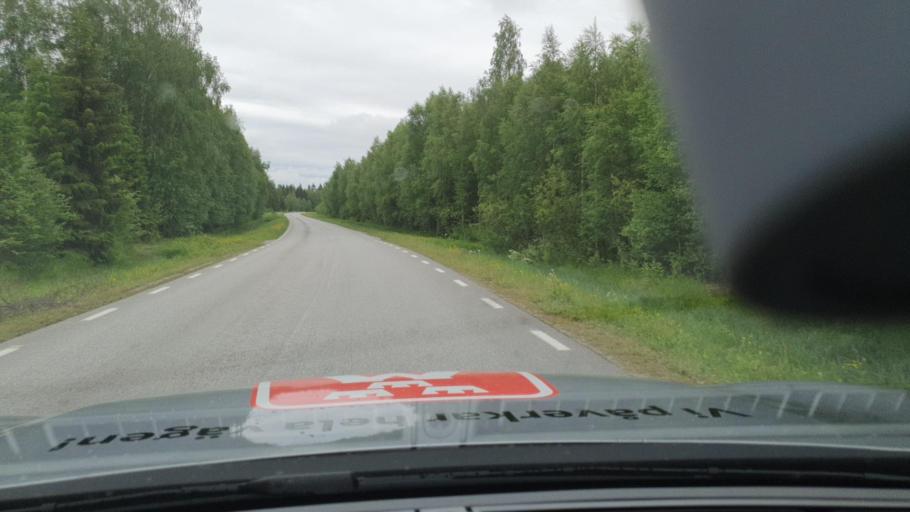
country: SE
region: Norrbotten
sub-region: Kalix Kommun
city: Toere
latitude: 65.8560
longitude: 22.6772
